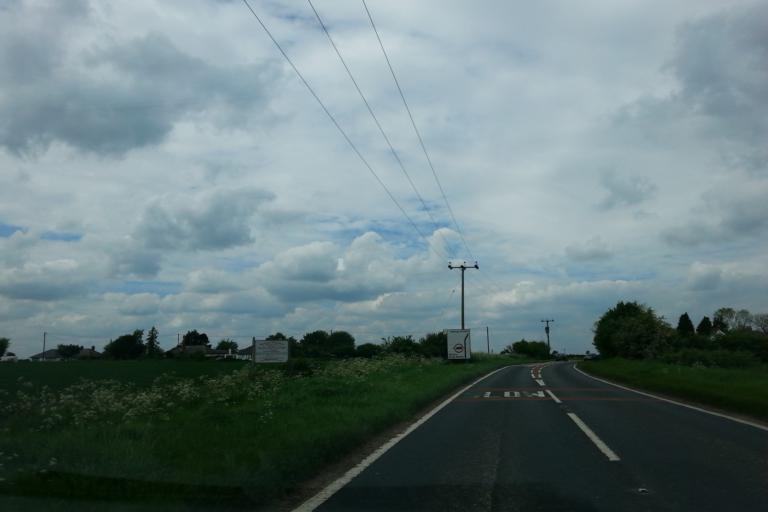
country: GB
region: England
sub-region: Cambridgeshire
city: Warboys
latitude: 52.4147
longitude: -0.1059
